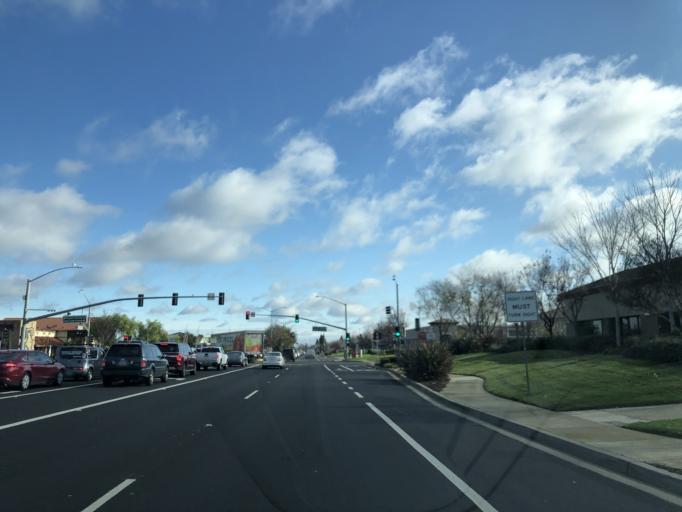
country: US
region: California
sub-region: Contra Costa County
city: Brentwood
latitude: 37.9434
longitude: -121.7387
